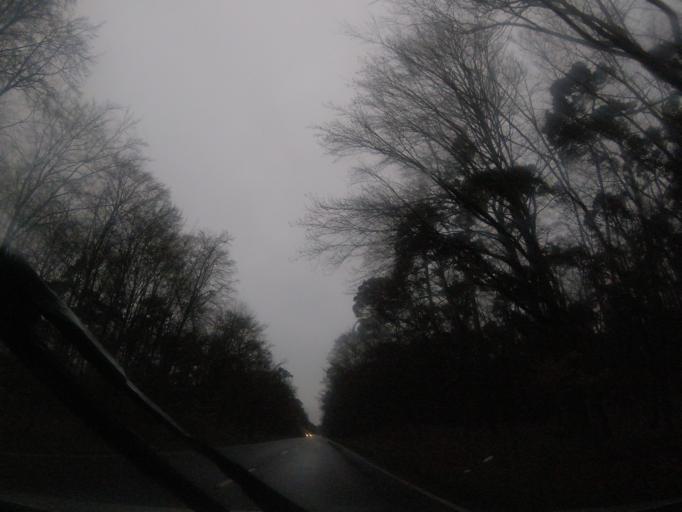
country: DE
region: Hesse
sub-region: Regierungsbezirk Darmstadt
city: Nauheim
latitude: 49.9788
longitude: 8.5005
